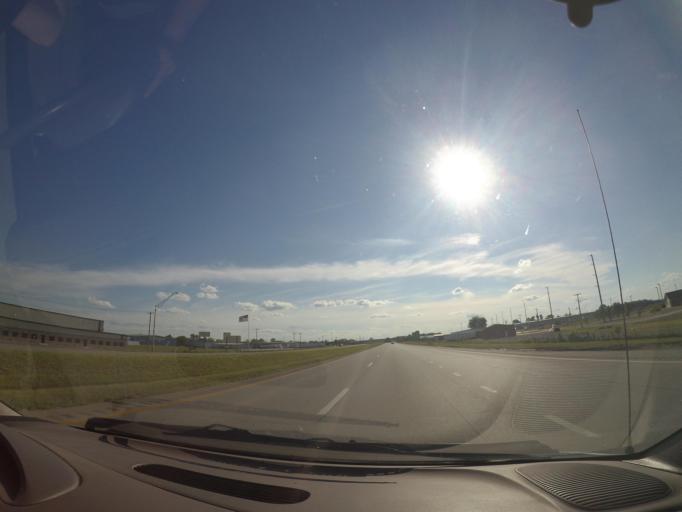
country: US
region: Ohio
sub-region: Henry County
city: Napoleon
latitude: 41.4132
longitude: -84.1118
